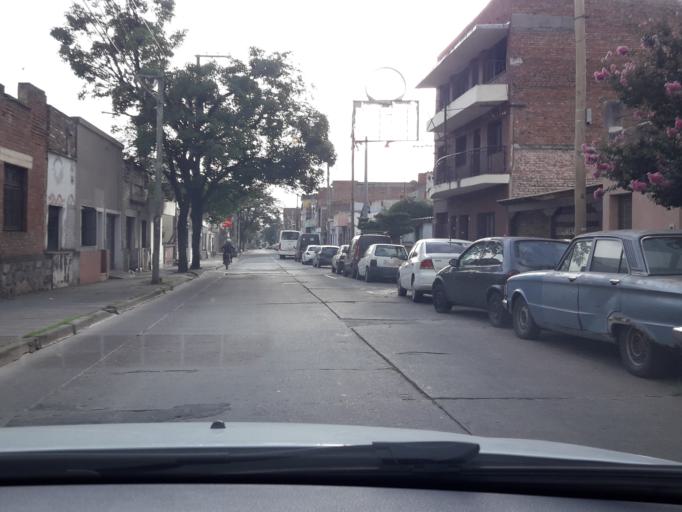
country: AR
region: Jujuy
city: San Salvador de Jujuy
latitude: -24.1908
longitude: -65.3074
